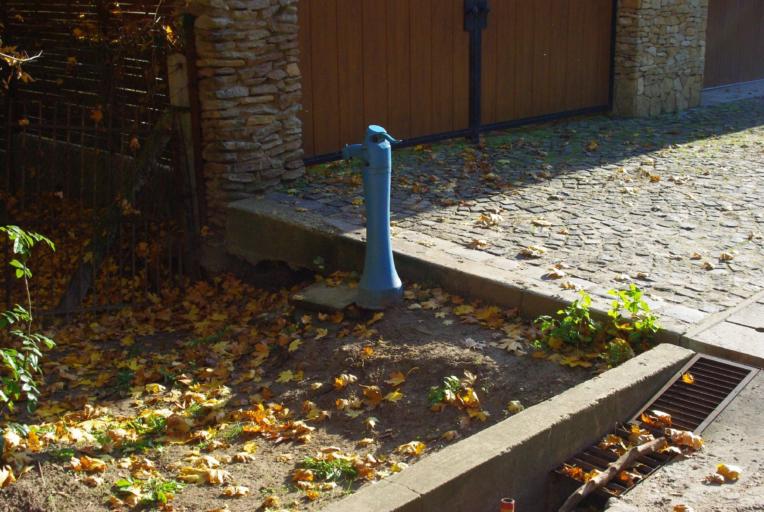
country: HU
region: Pest
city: Piliscsaba
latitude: 47.6432
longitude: 18.8362
